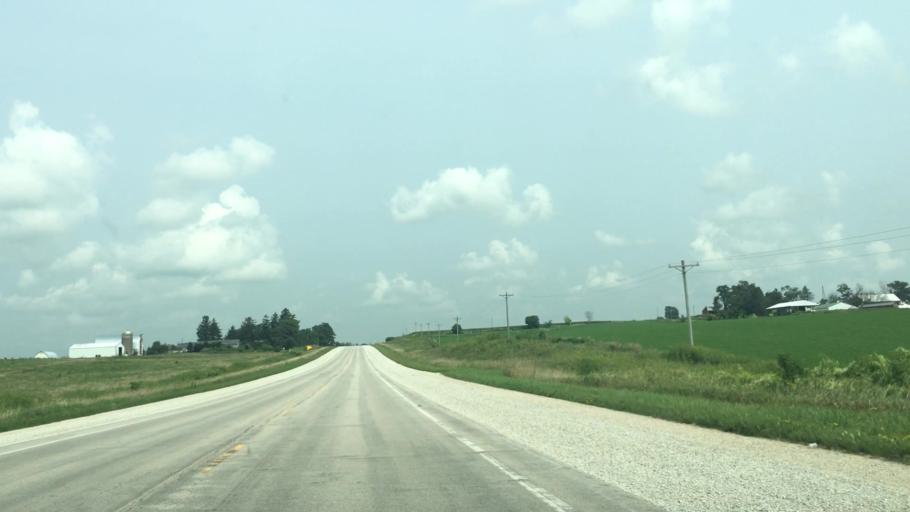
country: US
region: Iowa
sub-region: Winneshiek County
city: Decorah
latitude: 43.4162
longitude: -91.8592
